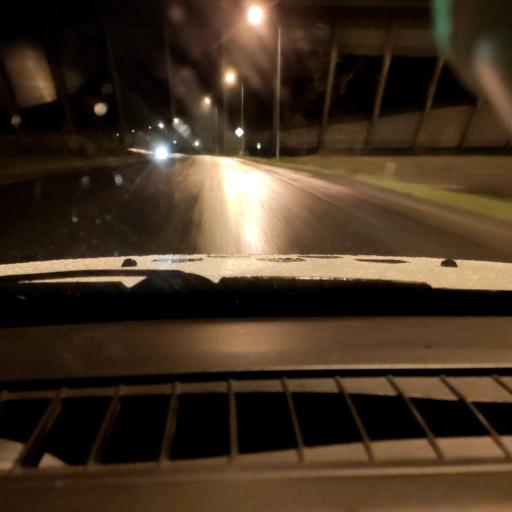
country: RU
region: Udmurtiya
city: Khokhryaki
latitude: 57.1742
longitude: 53.1589
